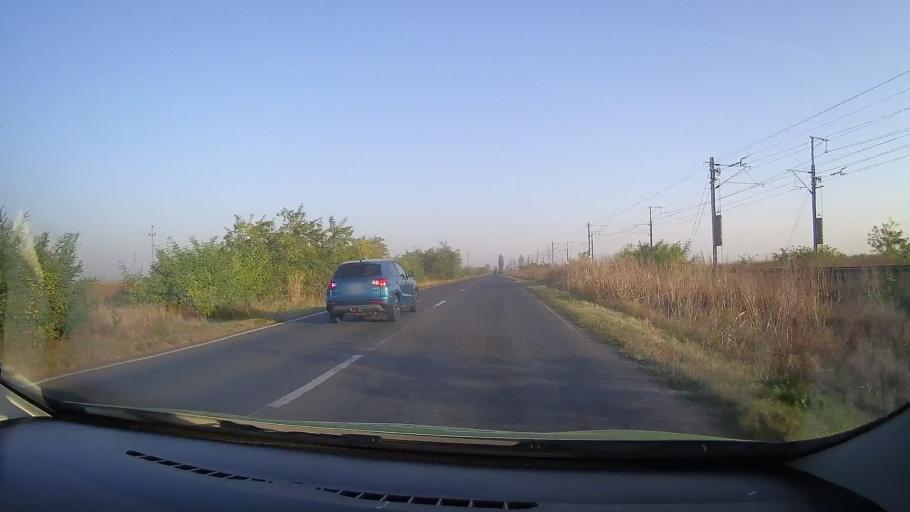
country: RO
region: Arad
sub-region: Comuna Sofronea
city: Sofronea
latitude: 46.2577
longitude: 21.3178
